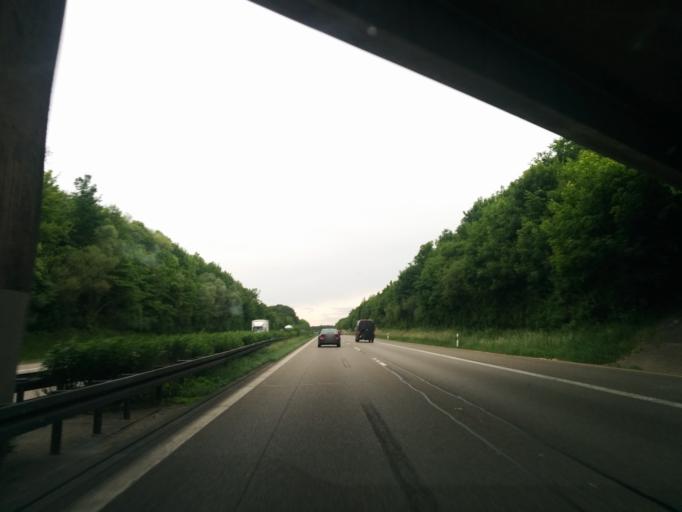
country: DE
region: Baden-Wuerttemberg
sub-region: Regierungsbezirk Stuttgart
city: Nattheim
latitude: 48.6661
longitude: 10.2296
